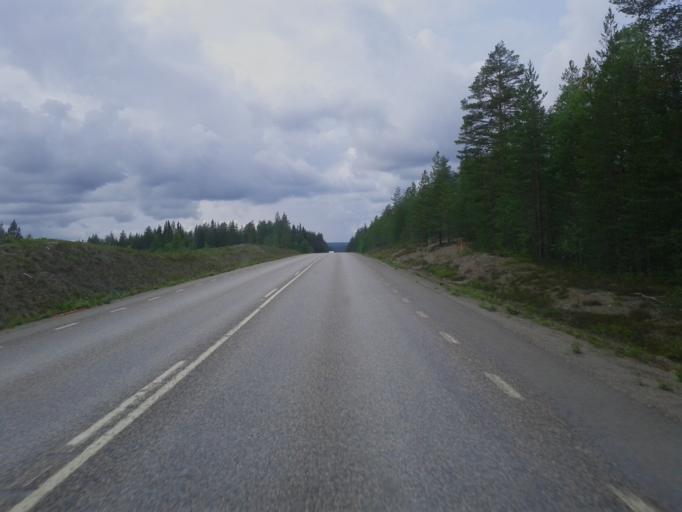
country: SE
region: Vaesterbotten
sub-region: Norsjo Kommun
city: Norsjoe
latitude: 64.9832
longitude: 19.5343
